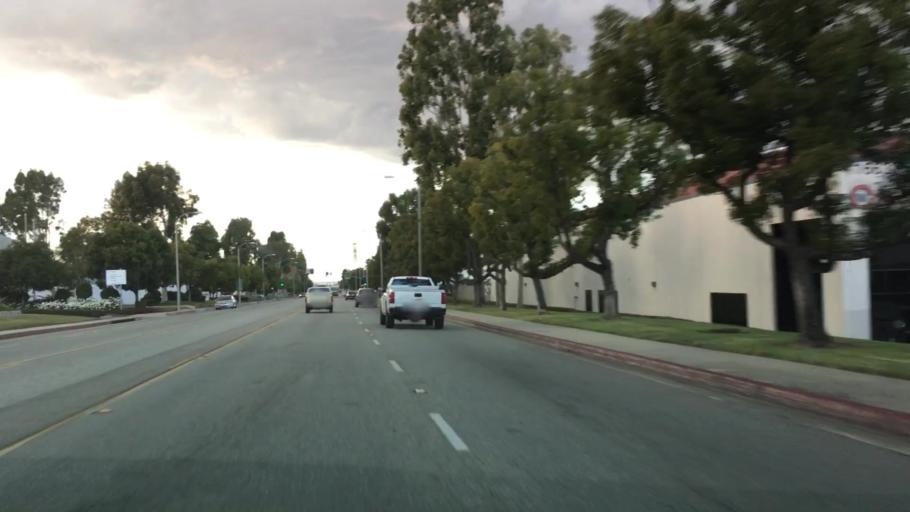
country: US
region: California
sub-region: Los Angeles County
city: La Puente
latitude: 34.0037
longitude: -117.9423
